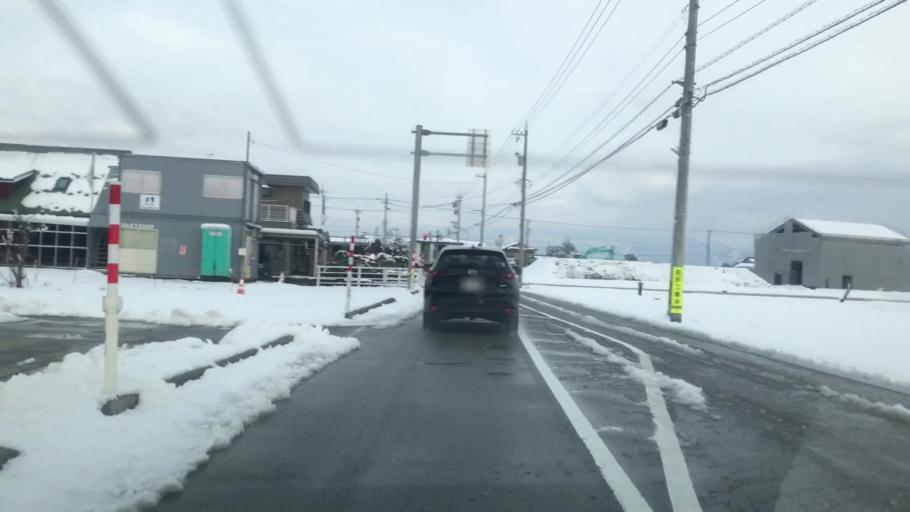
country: JP
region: Toyama
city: Toyama-shi
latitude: 36.6673
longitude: 137.2692
